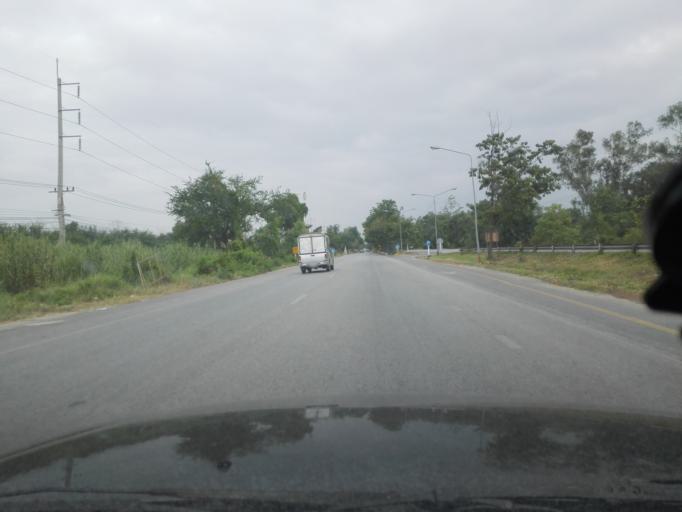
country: TH
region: Nakhon Sawan
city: Nakhon Sawan
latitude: 15.7284
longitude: 100.0382
